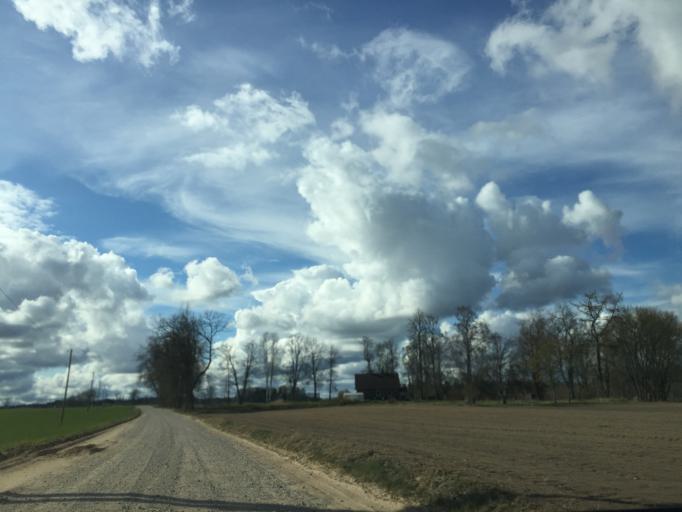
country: LV
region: Burtnieki
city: Matisi
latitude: 57.6097
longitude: 25.0367
